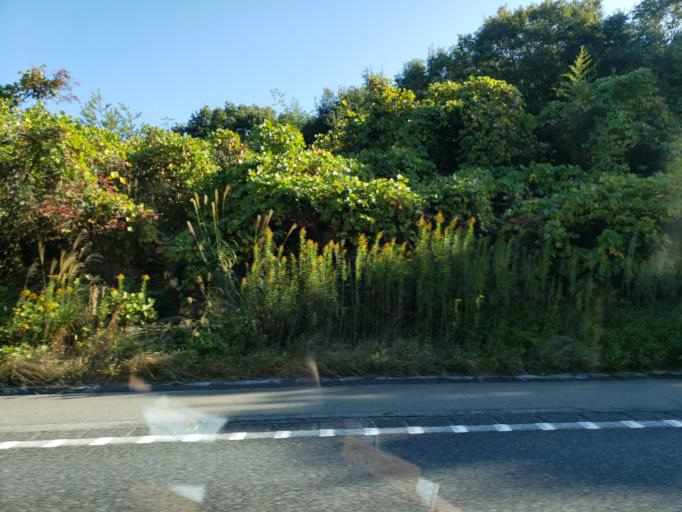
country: JP
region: Hyogo
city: Akashi
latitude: 34.6968
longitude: 134.9678
